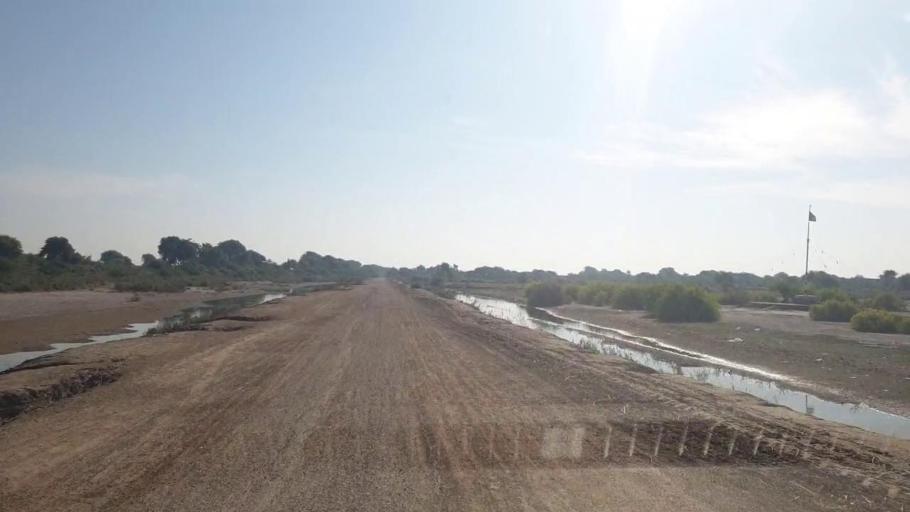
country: PK
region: Sindh
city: Rajo Khanani
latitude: 24.9720
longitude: 68.7878
